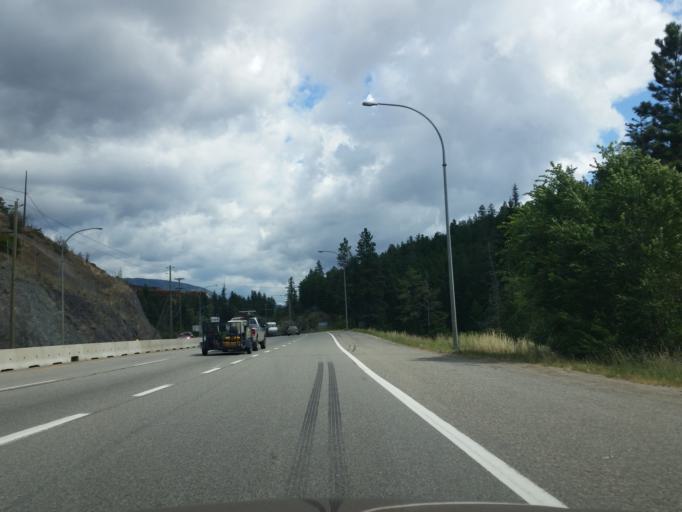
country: CA
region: British Columbia
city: Peachland
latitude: 49.8104
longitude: -119.6601
